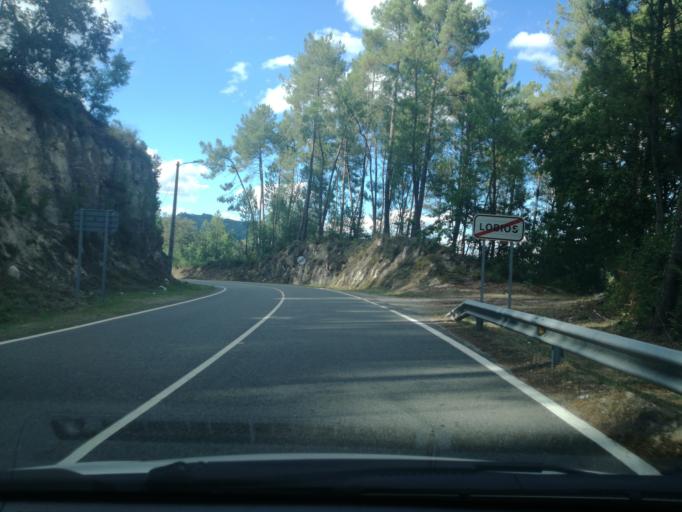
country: ES
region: Galicia
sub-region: Provincia de Ourense
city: Lobios
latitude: 41.9028
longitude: -8.0862
